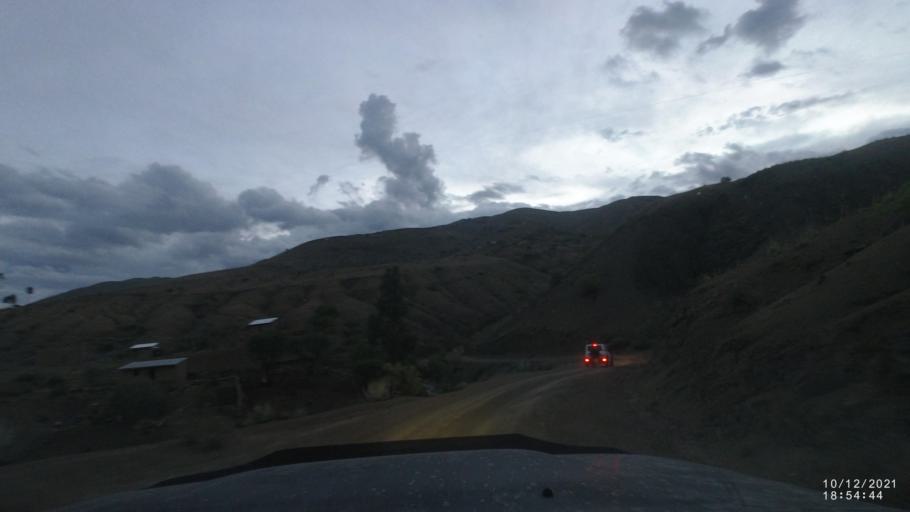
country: BO
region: Cochabamba
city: Tarata
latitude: -17.8860
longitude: -65.9591
